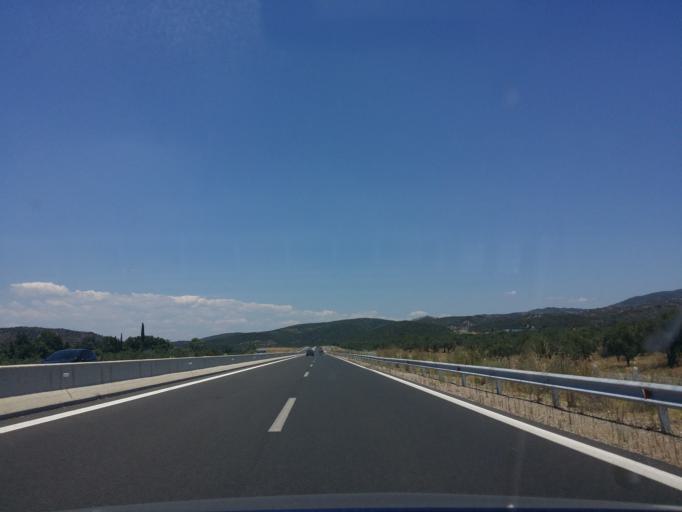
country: GR
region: Peloponnese
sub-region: Nomos Lakonias
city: Magoula
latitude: 37.1067
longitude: 22.4232
